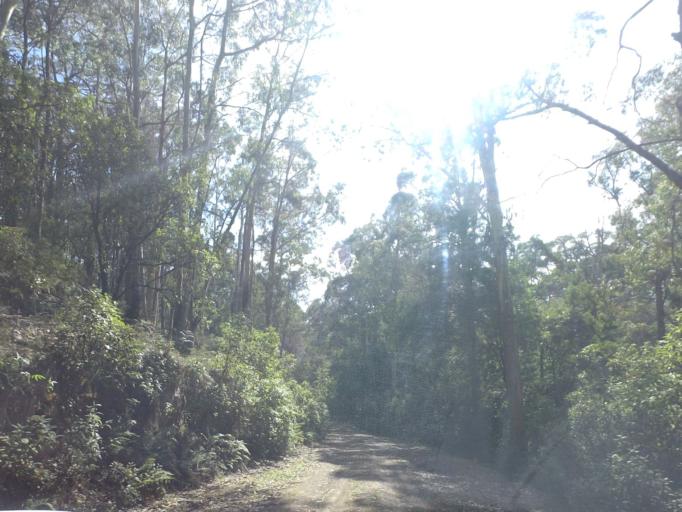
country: AU
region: Victoria
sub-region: Moorabool
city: Bacchus Marsh
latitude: -37.4286
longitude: 144.2360
